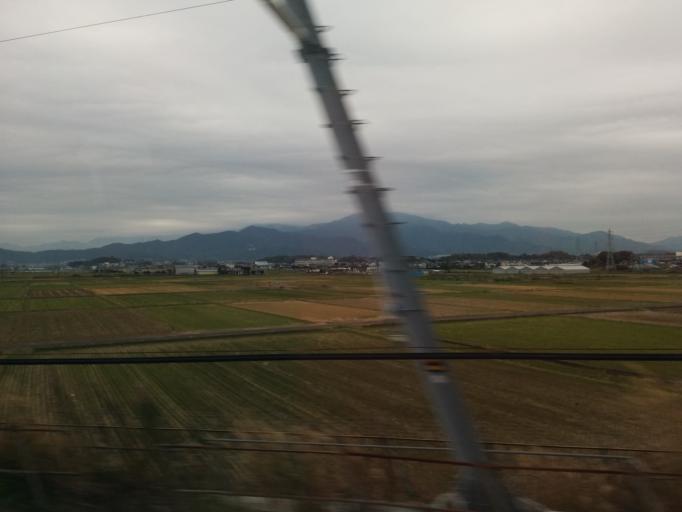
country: JP
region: Kanagawa
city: Isehara
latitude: 35.3655
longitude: 139.3340
